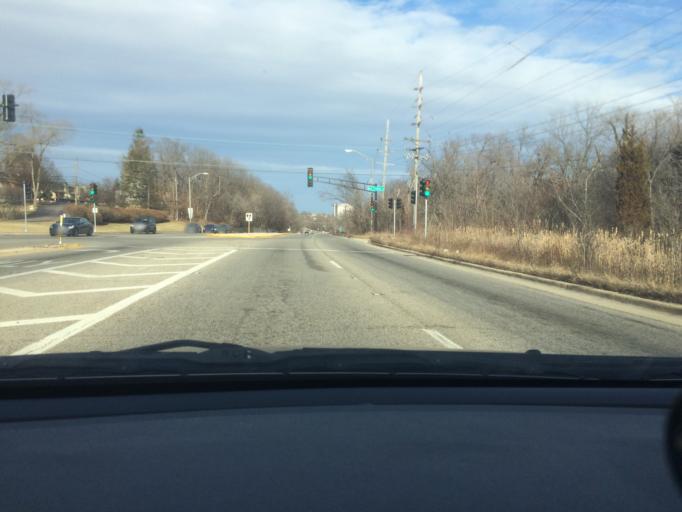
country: US
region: Illinois
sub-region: Kane County
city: Elgin
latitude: 42.0578
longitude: -88.2945
